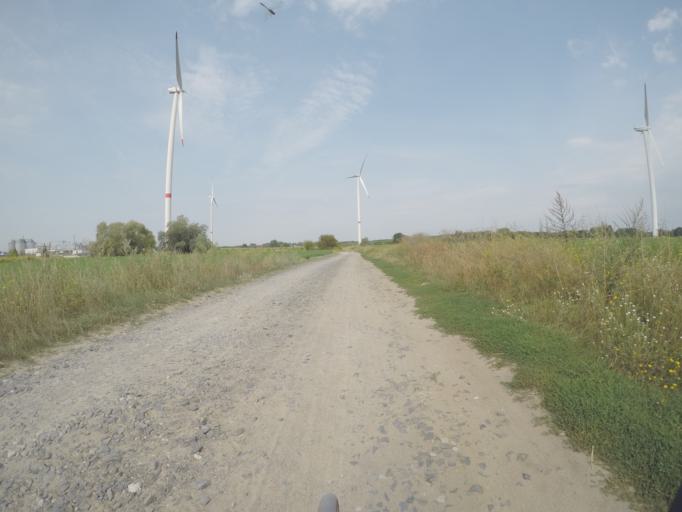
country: DE
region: Berlin
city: Blankenfelde
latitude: 52.6658
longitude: 13.4224
